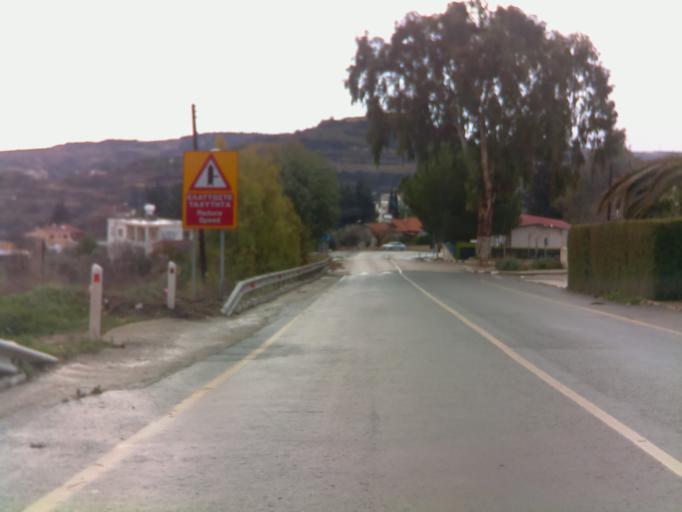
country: CY
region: Pafos
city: Tala
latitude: 34.8848
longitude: 32.4824
